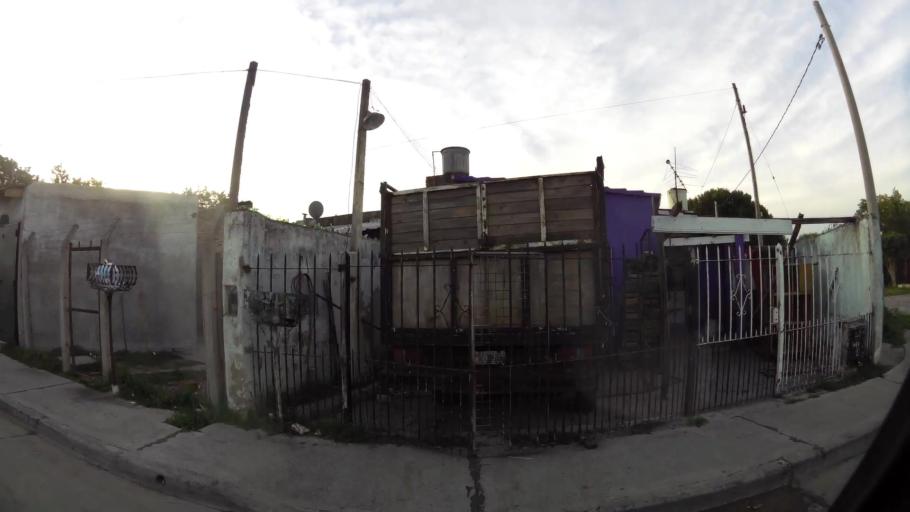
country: AR
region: Buenos Aires
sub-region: Partido de Almirante Brown
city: Adrogue
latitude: -34.7814
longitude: -58.3395
